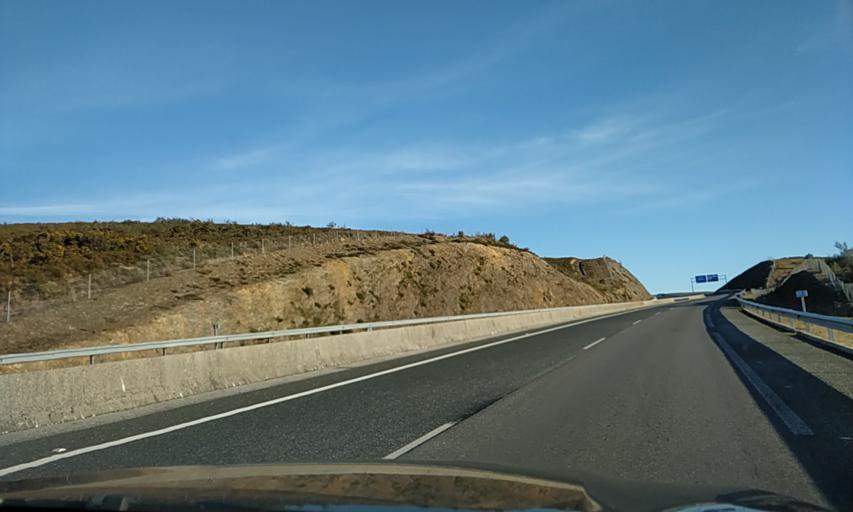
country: ES
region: Galicia
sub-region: Provincia de Pontevedra
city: Dozon
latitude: 42.5844
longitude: -8.0714
